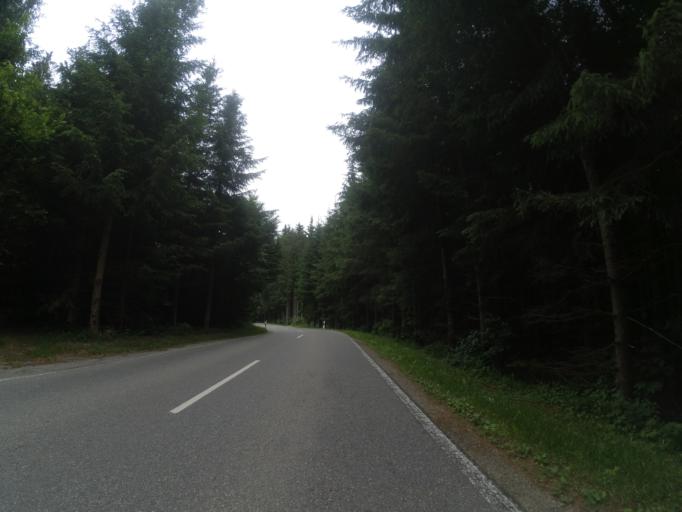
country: DE
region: Bavaria
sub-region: Swabia
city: Gestratz
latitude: 47.6963
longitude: 9.9717
